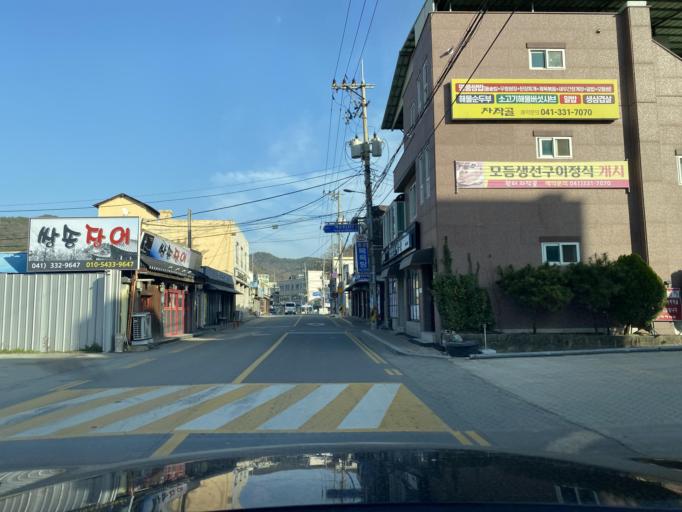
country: KR
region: Chungcheongnam-do
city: Yesan
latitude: 36.6801
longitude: 126.8503
